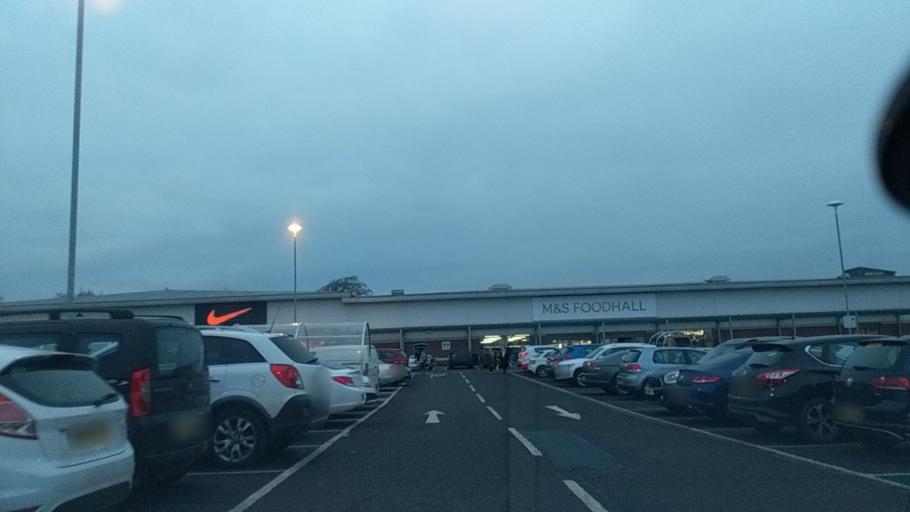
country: GB
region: Scotland
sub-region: South Lanarkshire
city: East Kilbride
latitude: 55.7836
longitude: -4.1691
